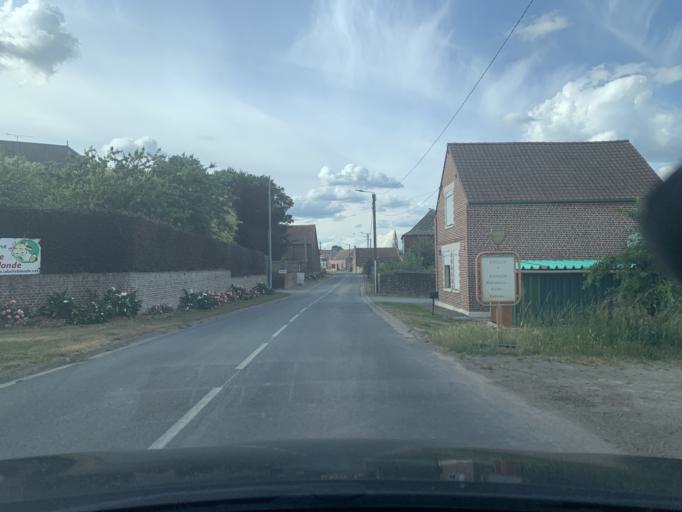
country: FR
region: Nord-Pas-de-Calais
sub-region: Departement du Nord
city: Gouzeaucourt
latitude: 50.0755
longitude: 3.1345
